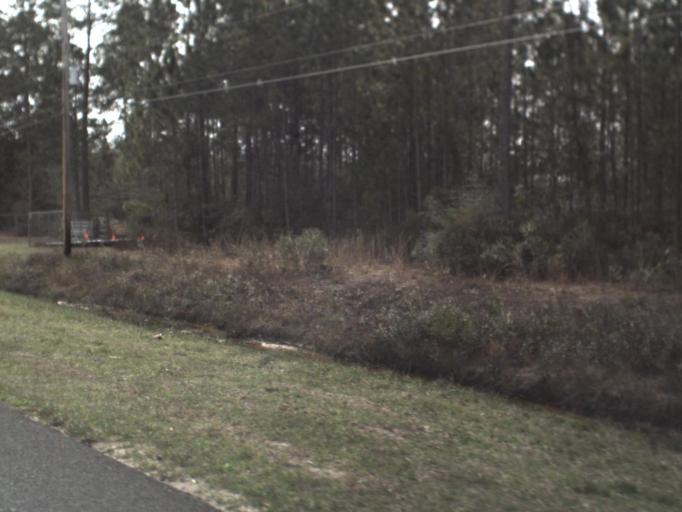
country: US
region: Florida
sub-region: Bay County
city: Youngstown
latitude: 30.5062
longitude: -85.4126
